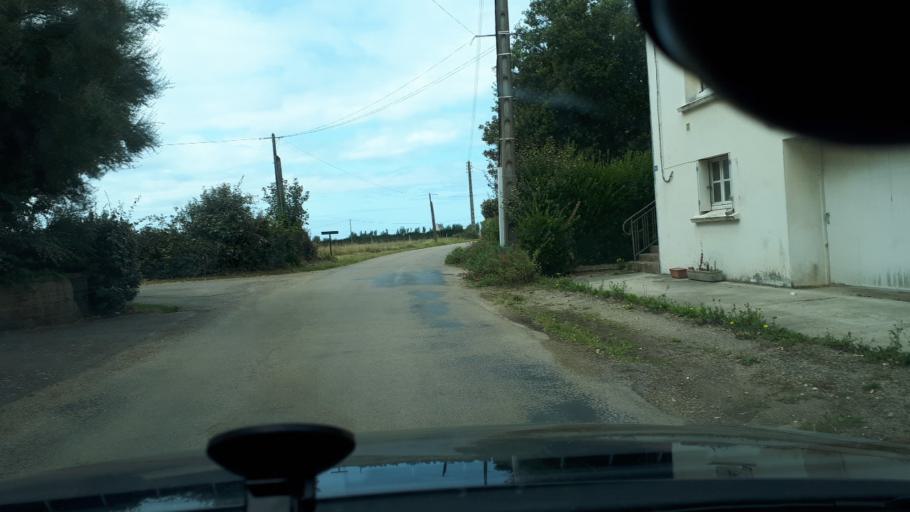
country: FR
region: Brittany
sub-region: Departement du Finistere
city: Pouldreuzic
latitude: 47.9606
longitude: -4.3897
